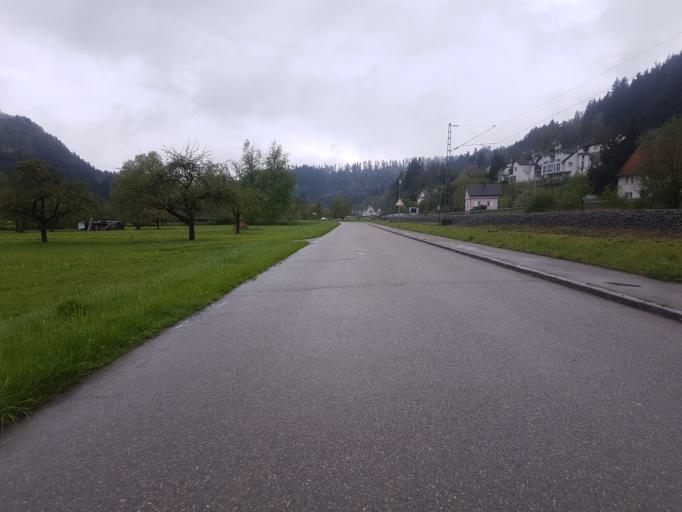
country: DE
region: Baden-Wuerttemberg
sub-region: Freiburg Region
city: Epfendorf
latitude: 48.2442
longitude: 8.5997
